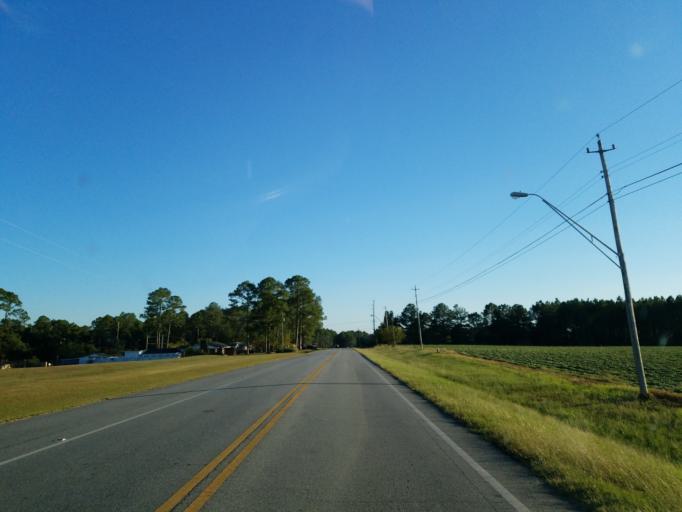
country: US
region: Georgia
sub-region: Worth County
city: Sylvester
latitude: 31.5466
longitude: -83.8431
